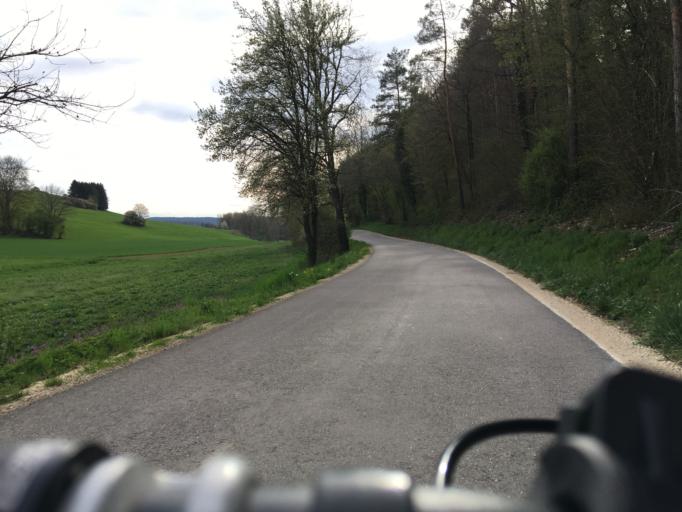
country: DE
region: Baden-Wuerttemberg
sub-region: Freiburg Region
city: Neuhausen
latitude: 47.8088
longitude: 8.7485
